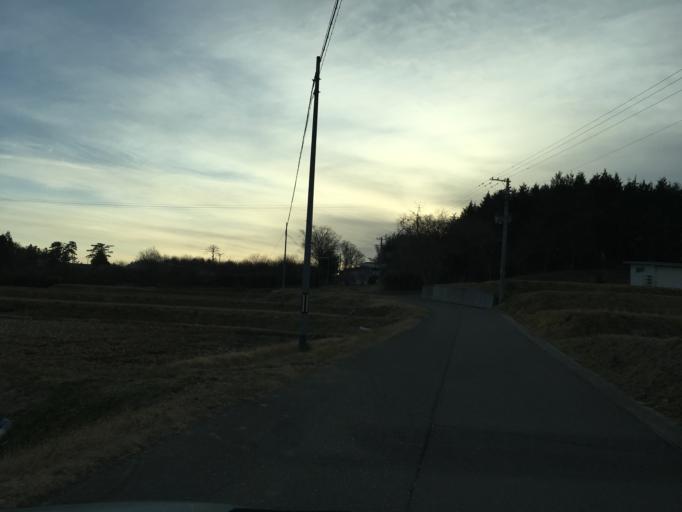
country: JP
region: Miyagi
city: Kogota
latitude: 38.6747
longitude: 141.0888
